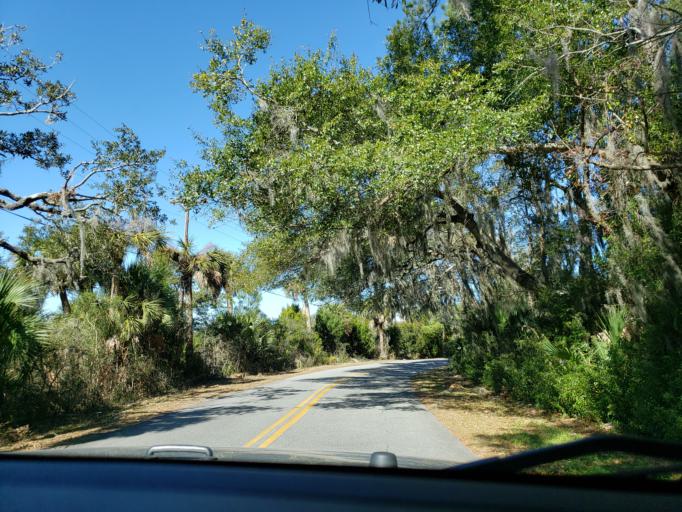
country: US
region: Georgia
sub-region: Chatham County
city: Whitemarsh Island
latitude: 32.0517
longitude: -81.0086
